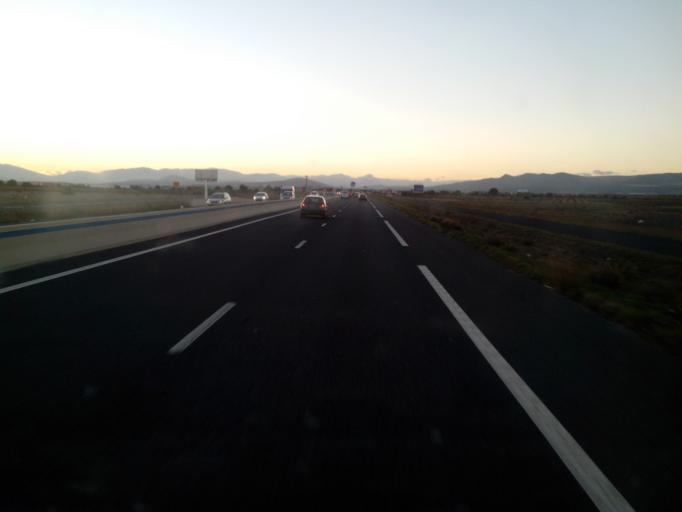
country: FR
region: Languedoc-Roussillon
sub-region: Departement des Pyrenees-Orientales
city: Claira
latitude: 42.7775
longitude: 2.9329
